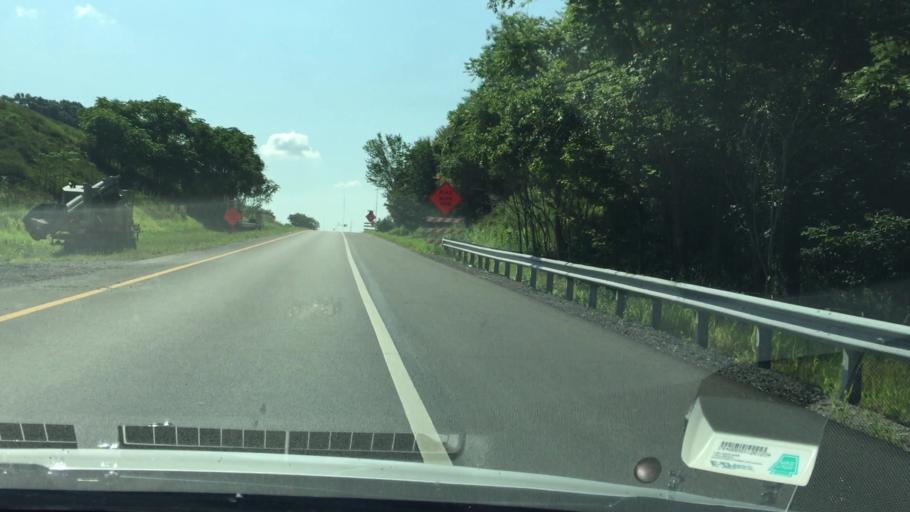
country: US
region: Pennsylvania
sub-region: Allegheny County
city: Avalon
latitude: 40.5132
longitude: -80.0540
